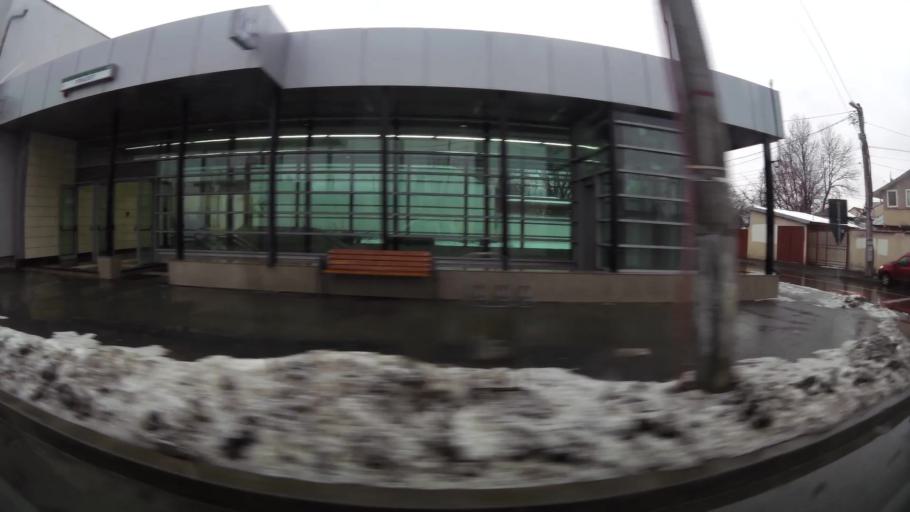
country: RO
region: Ilfov
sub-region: Comuna Mogosoaia
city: Mogosoaia
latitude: 44.5005
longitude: 26.0270
